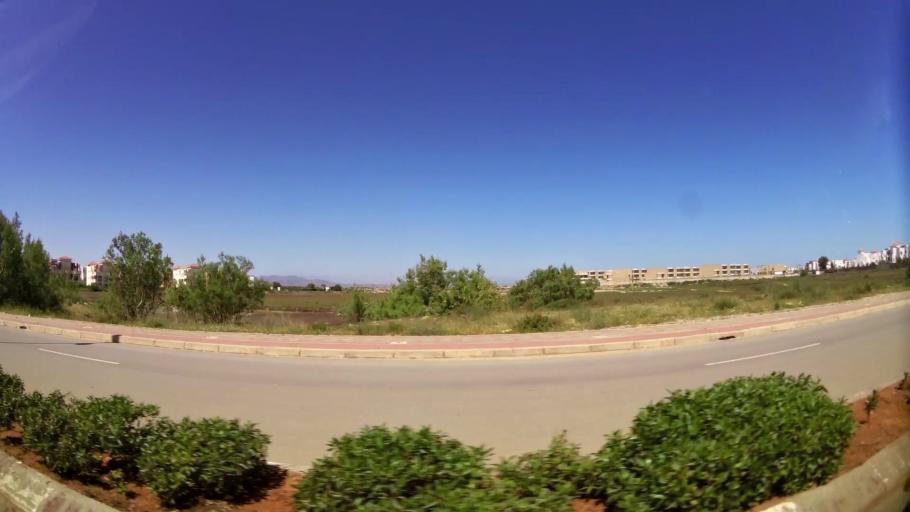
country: MA
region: Oriental
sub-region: Berkane-Taourirt
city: Madagh
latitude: 35.1070
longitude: -2.3116
